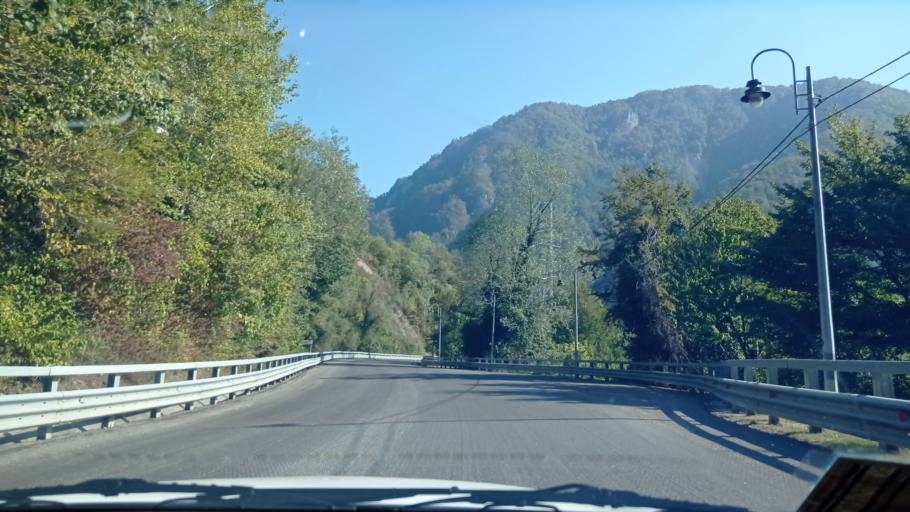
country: RU
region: Krasnodarskiy
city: Vysokoye
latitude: 43.5932
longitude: 40.0094
